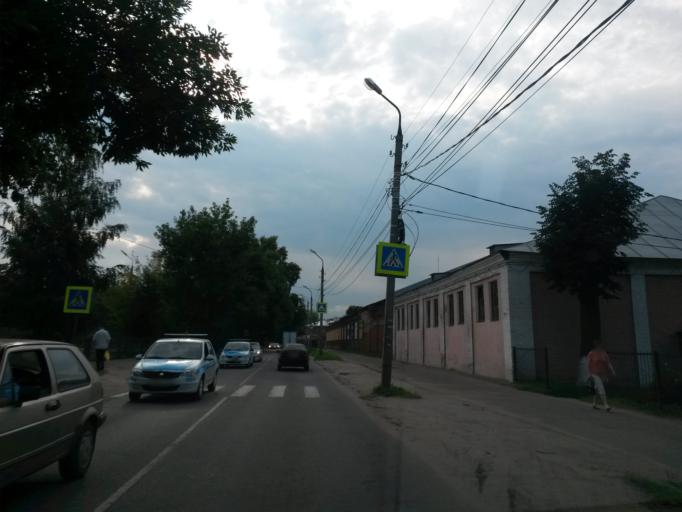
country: RU
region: Jaroslavl
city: Yaroslavl
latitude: 57.6084
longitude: 39.8336
